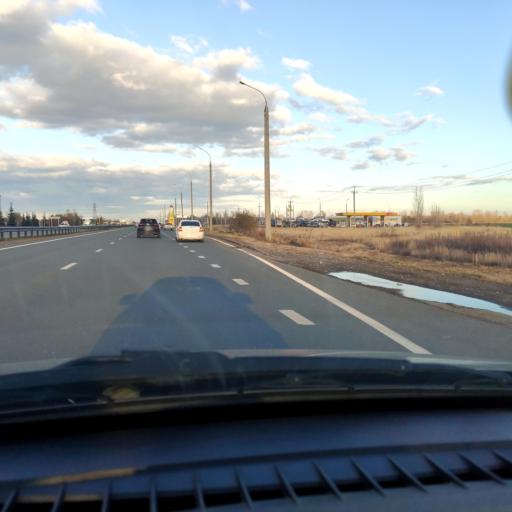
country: RU
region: Samara
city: Tol'yatti
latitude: 53.5575
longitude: 49.3514
